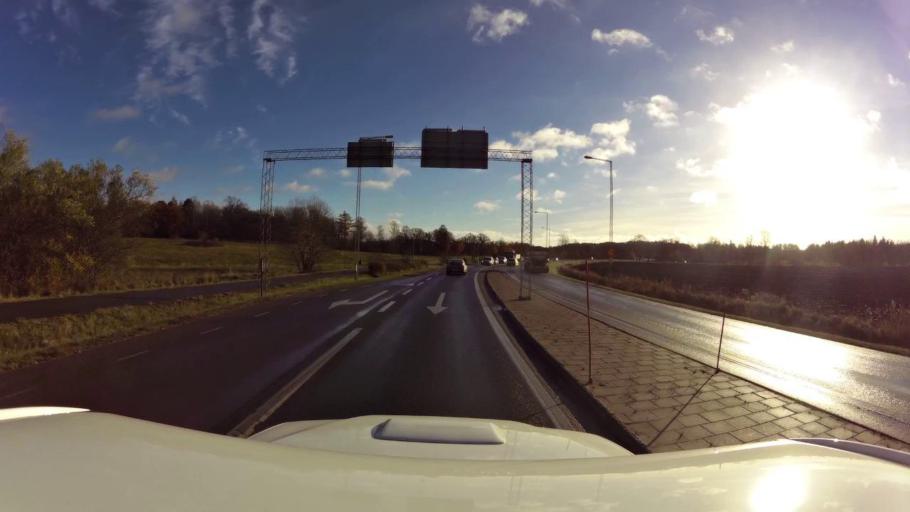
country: SE
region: OEstergoetland
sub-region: Linkopings Kommun
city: Linkoping
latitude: 58.3896
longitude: 15.6251
